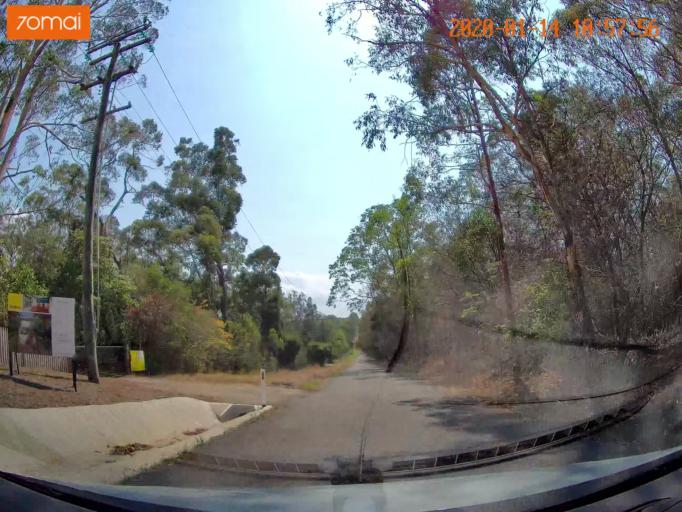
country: AU
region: New South Wales
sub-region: Lake Macquarie Shire
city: Dora Creek
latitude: -33.0999
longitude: 151.4899
